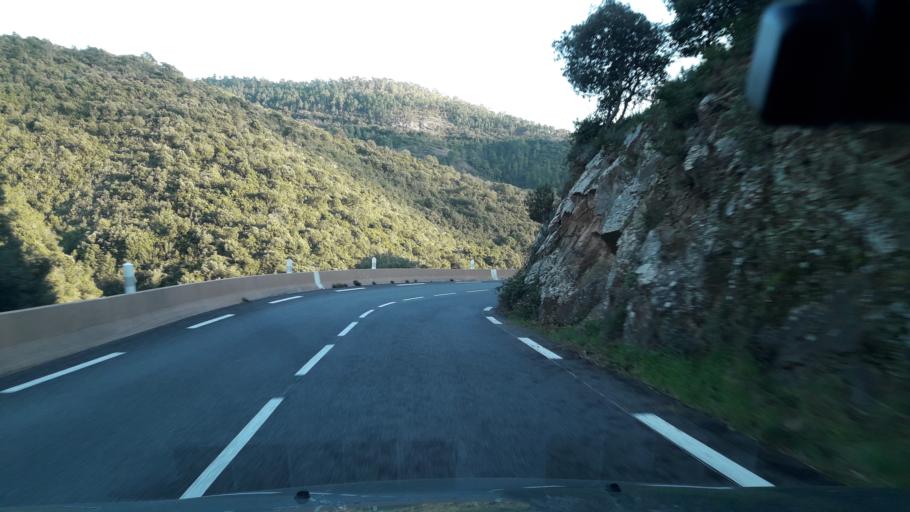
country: FR
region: Provence-Alpes-Cote d'Azur
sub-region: Departement du Var
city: Saint-Raphael
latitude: 43.4902
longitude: 6.7795
